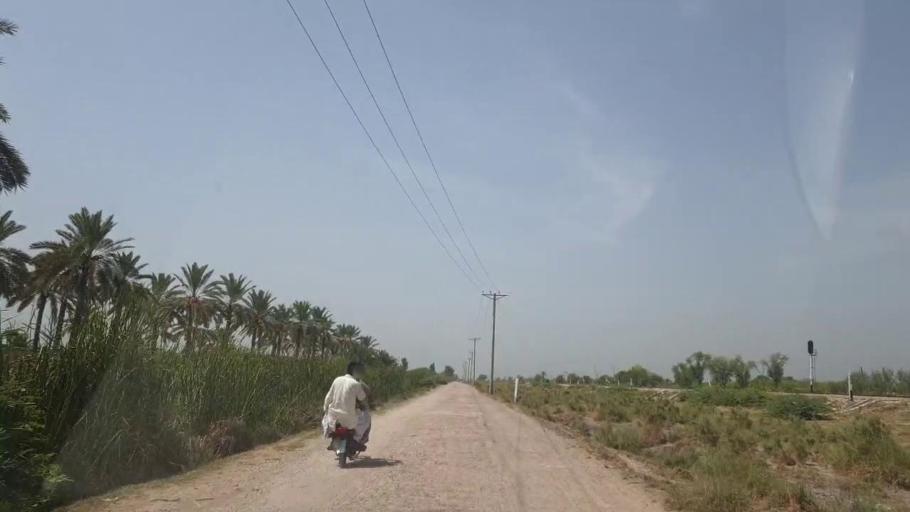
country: PK
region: Sindh
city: Gambat
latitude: 27.3322
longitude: 68.5418
